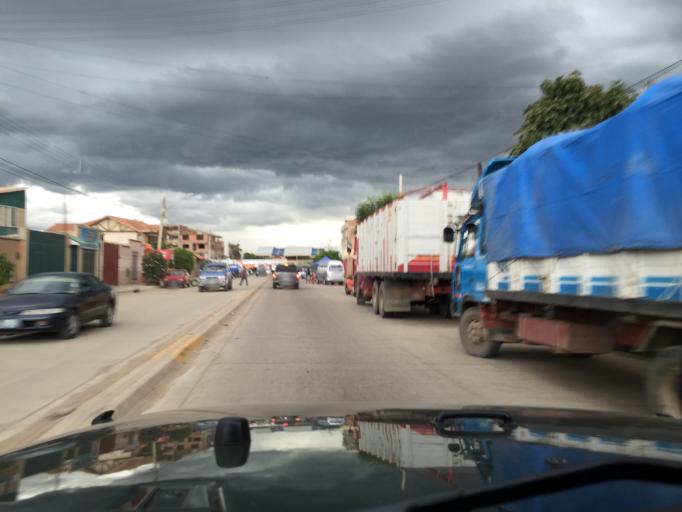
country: BO
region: Cochabamba
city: Cochabamba
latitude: -17.4010
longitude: -66.1851
